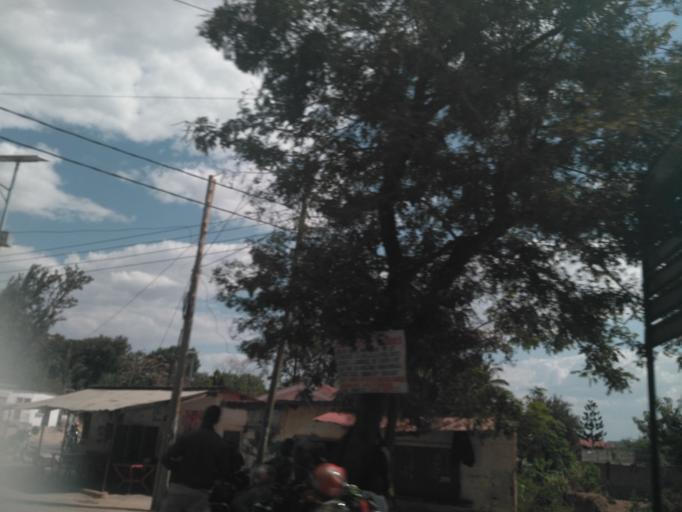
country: TZ
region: Mwanza
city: Mwanza
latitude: -2.5062
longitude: 32.9107
